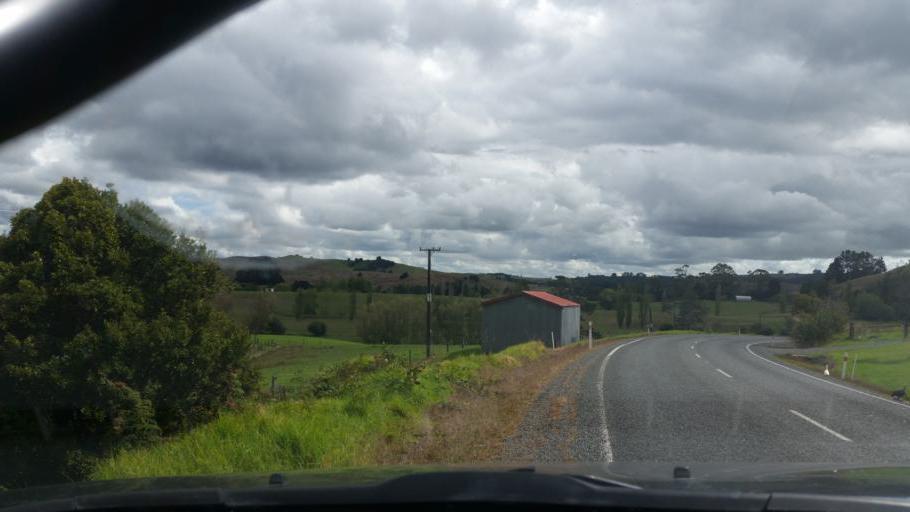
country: NZ
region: Northland
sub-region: Whangarei
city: Ruakaka
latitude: -35.9528
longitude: 174.2932
